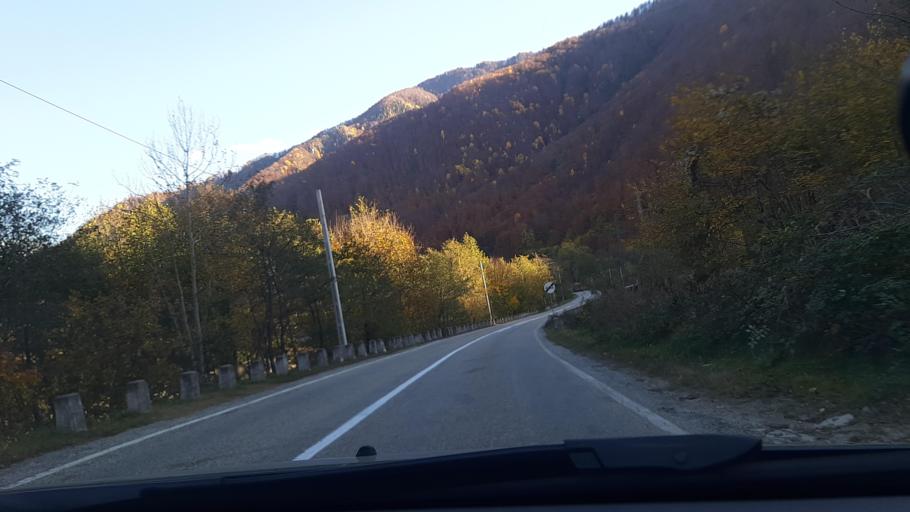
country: RO
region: Valcea
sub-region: Comuna Brezoi
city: Brezoi
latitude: 45.3518
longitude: 24.1563
